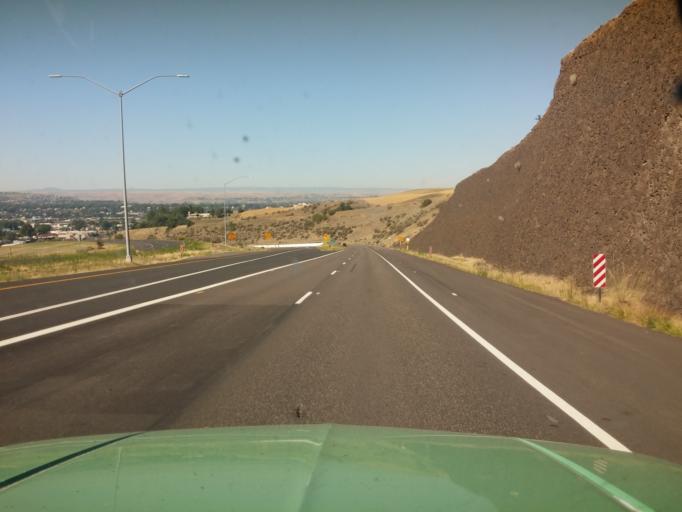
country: US
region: Idaho
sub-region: Nez Perce County
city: Lewiston
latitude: 46.4349
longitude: -116.9912
